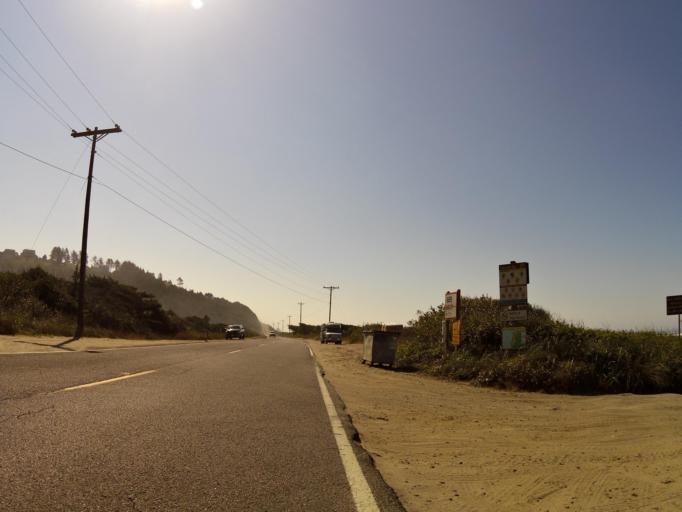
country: US
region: Oregon
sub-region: Tillamook County
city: Pacific City
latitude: 45.2461
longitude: -123.9673
